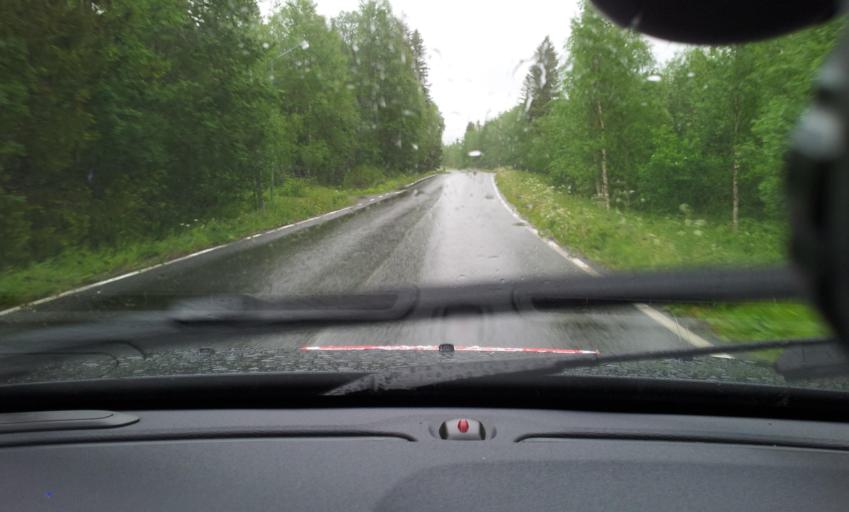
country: SE
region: Jaemtland
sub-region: Are Kommun
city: Are
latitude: 63.3157
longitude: 13.1135
